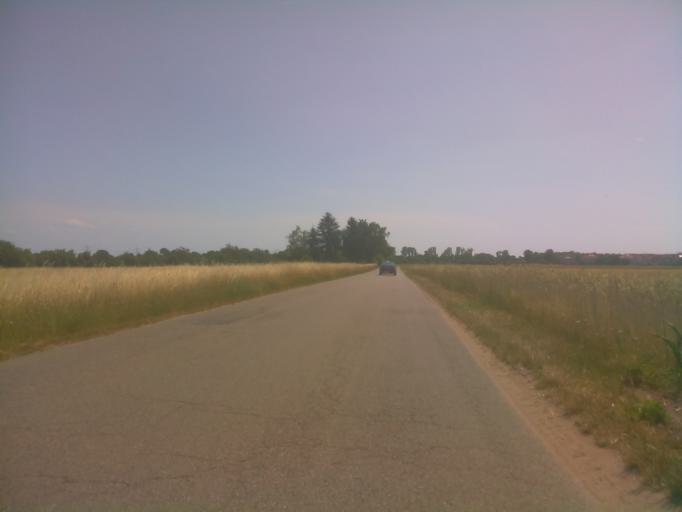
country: DE
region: Hesse
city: Viernheim
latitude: 49.5472
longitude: 8.6053
